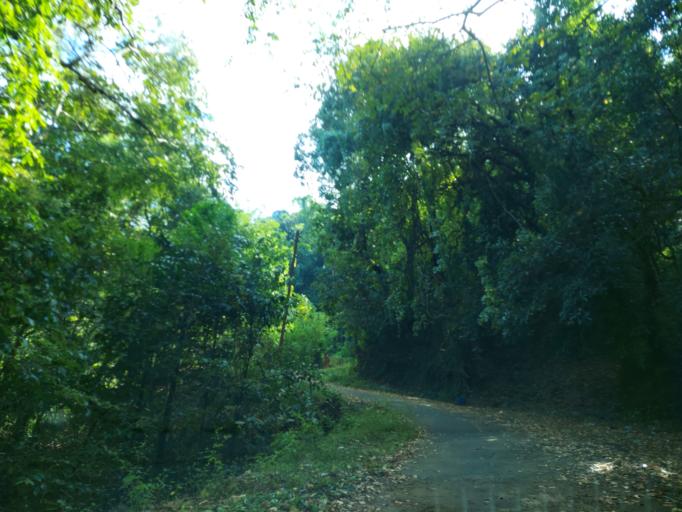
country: IN
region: Maharashtra
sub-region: Sindhudurg
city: Savantvadi
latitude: 15.9039
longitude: 73.8132
